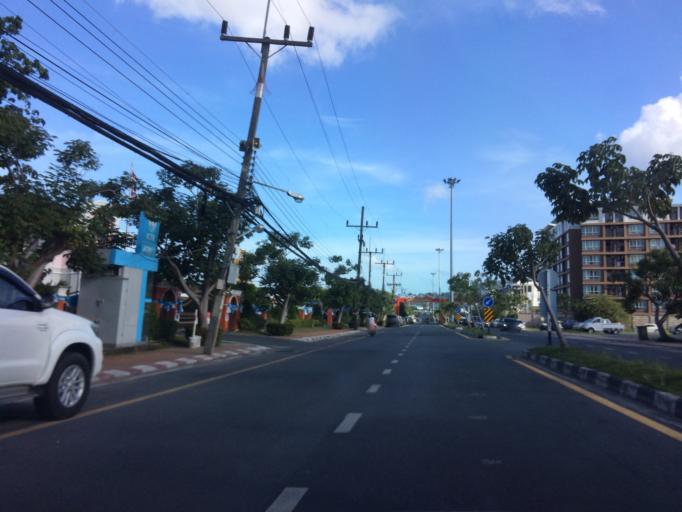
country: TH
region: Phuket
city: Kathu
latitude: 7.9116
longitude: 98.3470
